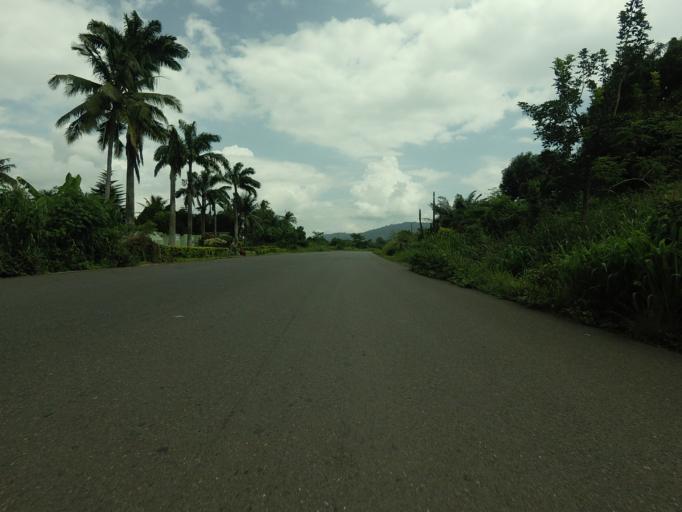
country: GH
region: Volta
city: Ho
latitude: 6.5427
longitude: 0.2476
